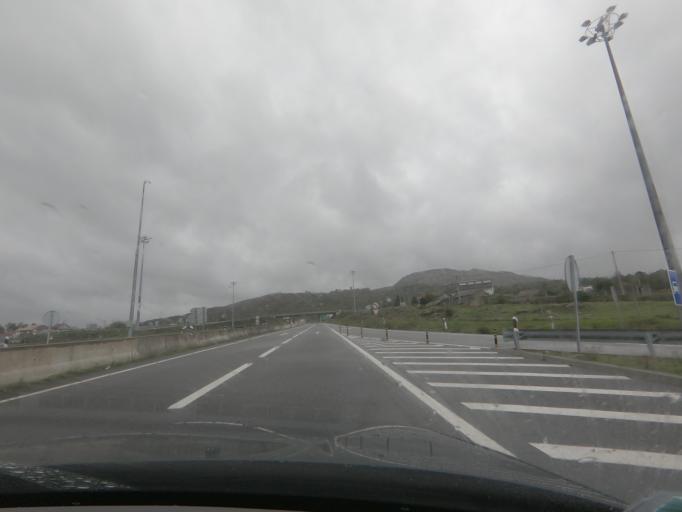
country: PT
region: Vila Real
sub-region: Vila Real
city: Vila Real
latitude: 41.2837
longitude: -7.8045
